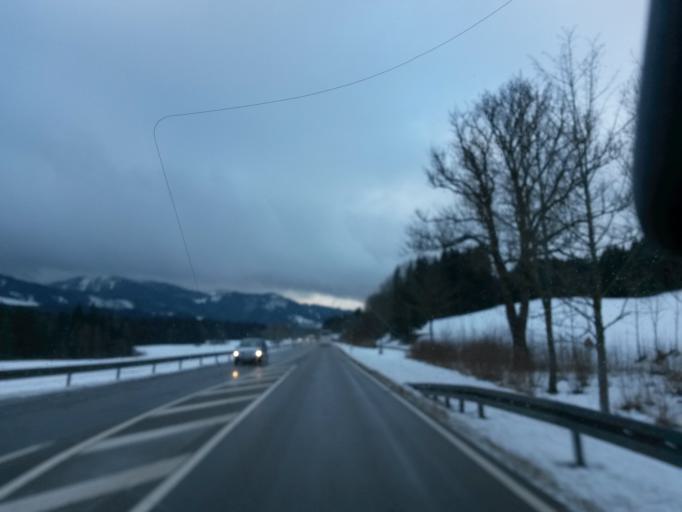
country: DE
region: Bavaria
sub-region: Swabia
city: Oy-Mittelberg
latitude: 47.6215
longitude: 10.4410
